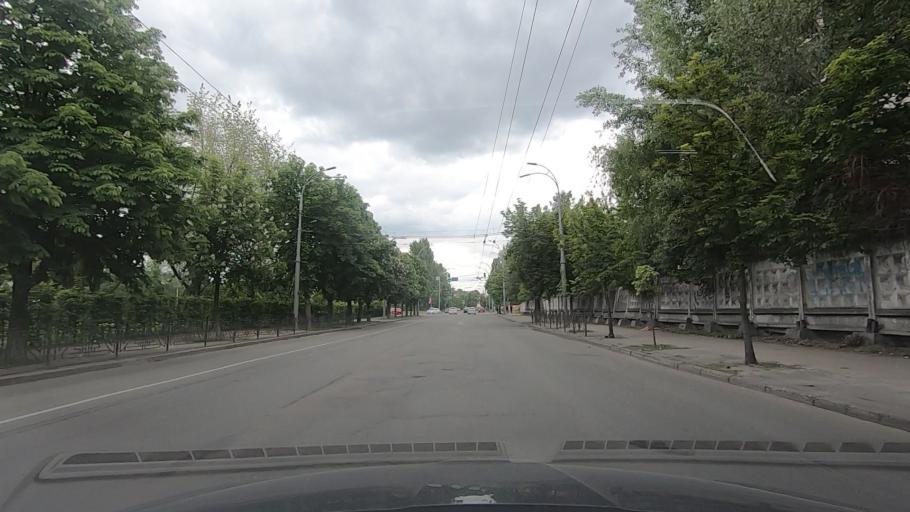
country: MD
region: Riscani
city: Riscani
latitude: 48.0521
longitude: 27.5900
